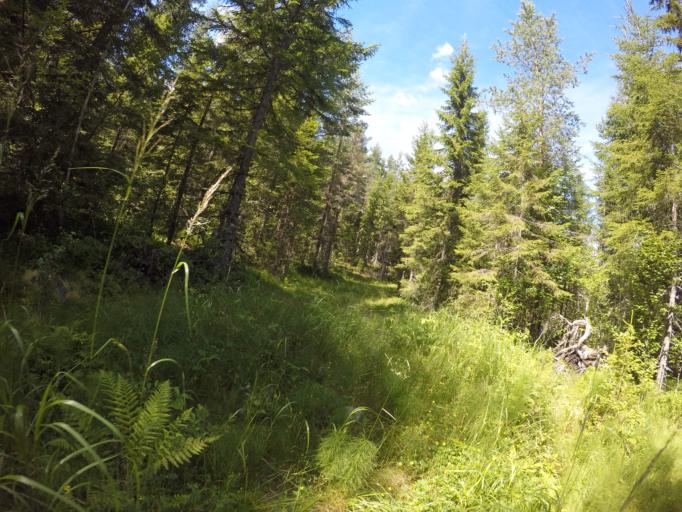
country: SE
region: Vaermland
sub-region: Filipstads Kommun
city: Lesjofors
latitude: 60.0915
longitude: 14.4698
